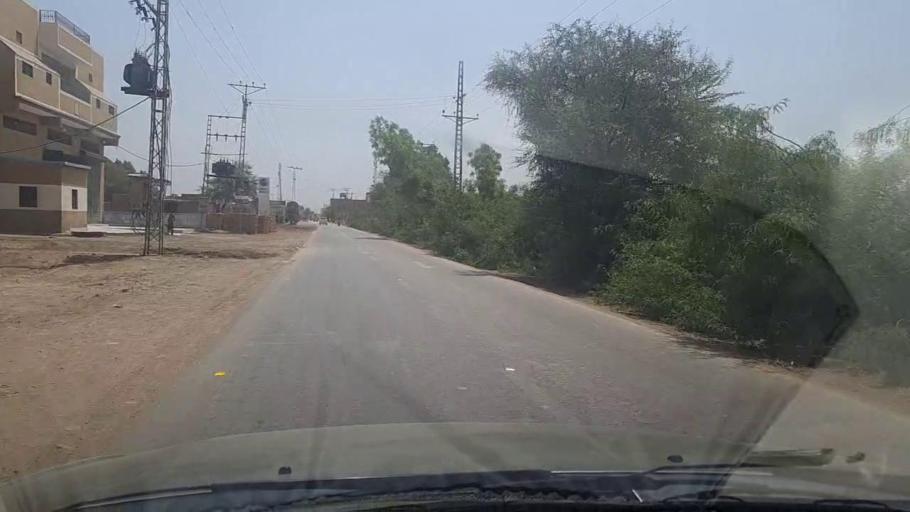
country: PK
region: Sindh
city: Hyderabad
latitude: 25.3881
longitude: 68.4229
